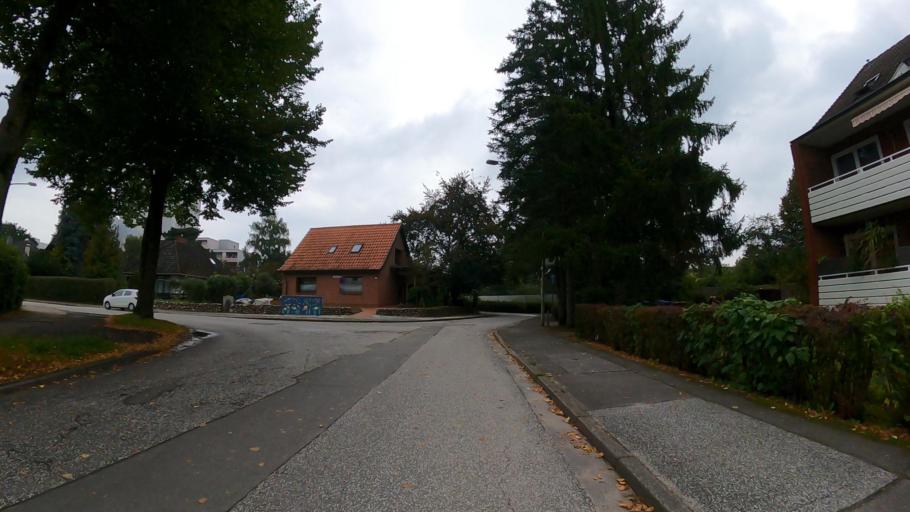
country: DE
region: Schleswig-Holstein
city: Rellingen
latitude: 53.6425
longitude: 9.8152
